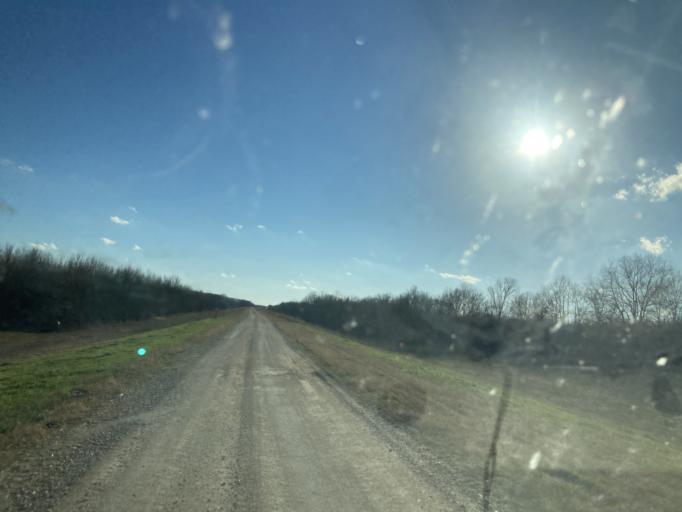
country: US
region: Mississippi
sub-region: Yazoo County
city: Yazoo City
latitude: 32.9306
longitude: -90.5488
